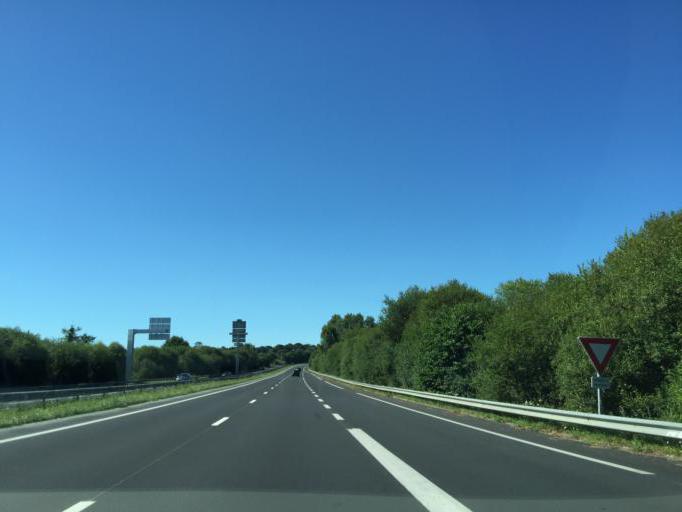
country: FR
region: Brittany
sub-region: Departement des Cotes-d'Armor
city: Saint-Samson-sur-Rance
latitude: 48.4802
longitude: -2.0441
